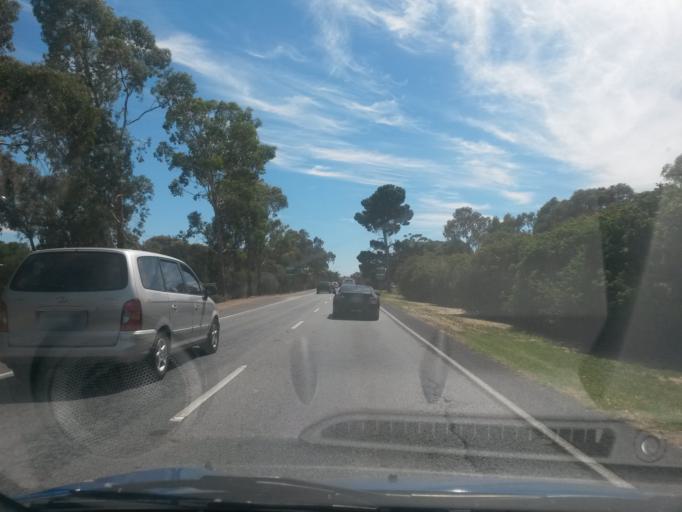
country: AU
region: South Australia
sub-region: Salisbury
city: Salisbury
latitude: -34.7776
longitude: 138.6593
